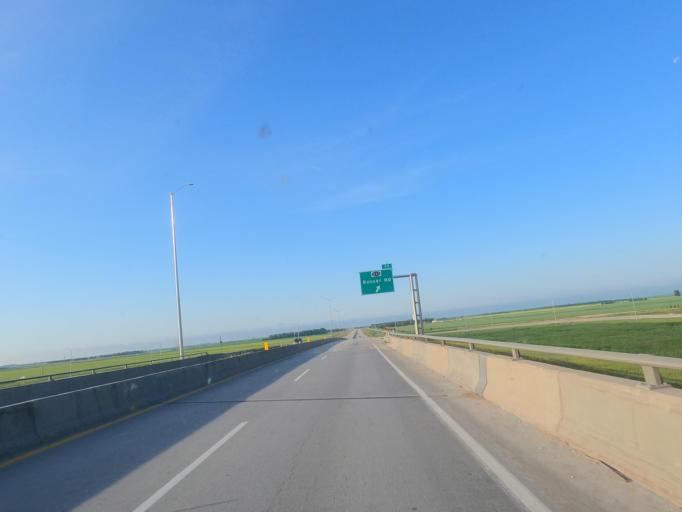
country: CA
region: Manitoba
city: Headingley
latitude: 49.9557
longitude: -97.3205
